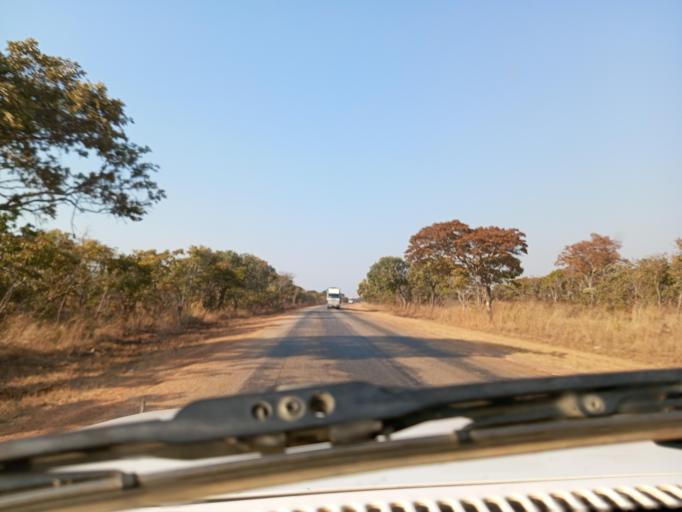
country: ZM
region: Northern
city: Mpika
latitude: -12.3691
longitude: 31.1030
